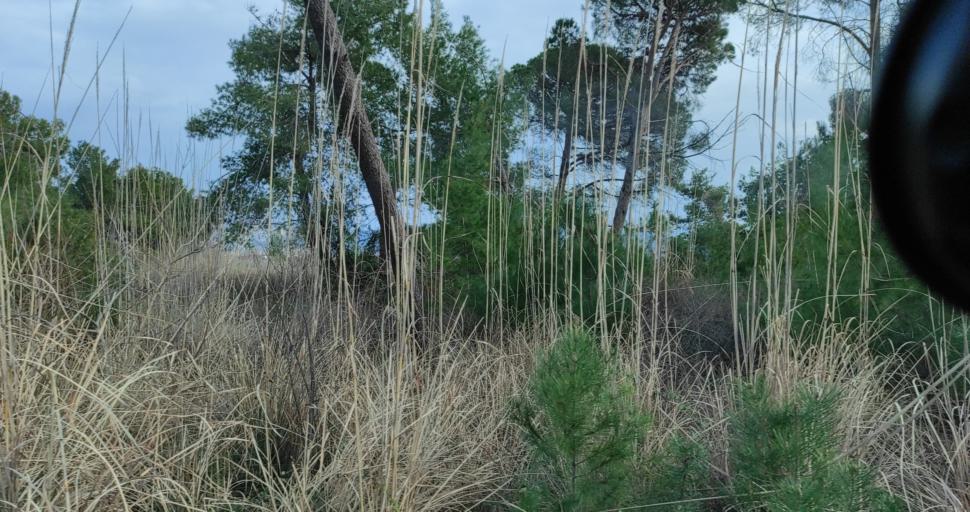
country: AL
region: Lezhe
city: Shengjin
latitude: 41.7653
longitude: 19.5969
